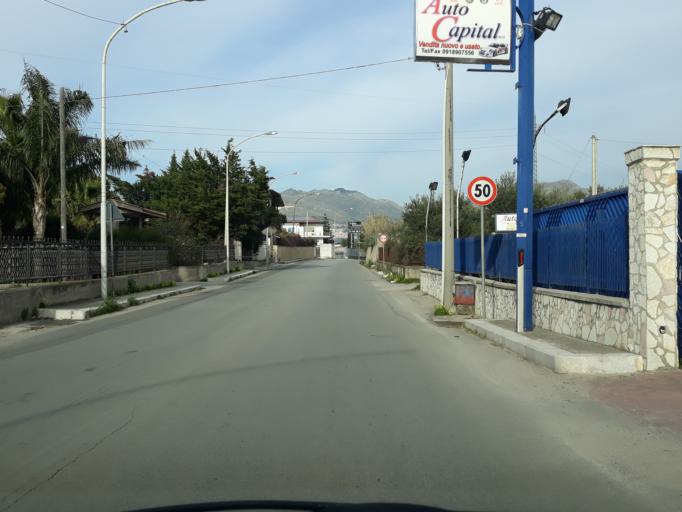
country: IT
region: Sicily
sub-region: Palermo
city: Partinico
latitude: 38.0561
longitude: 13.1305
